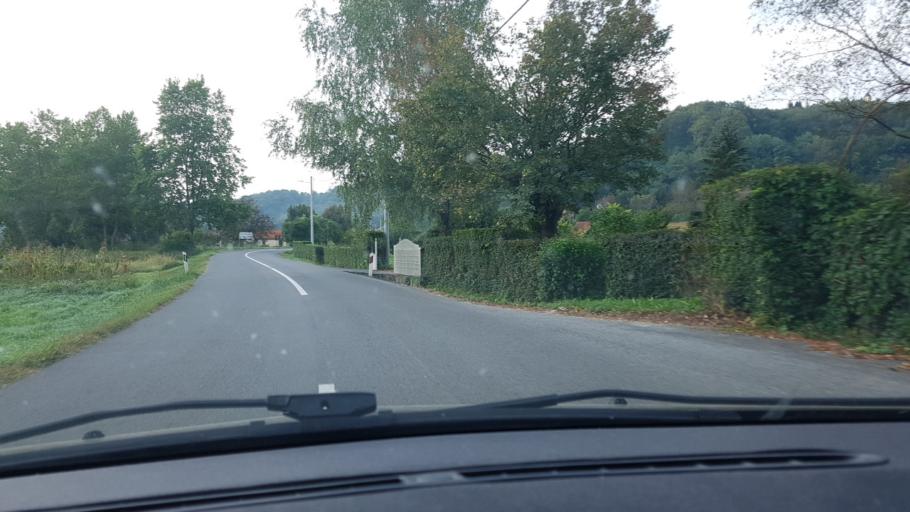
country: HR
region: Krapinsko-Zagorska
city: Mihovljan
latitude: 46.1108
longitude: 16.0103
